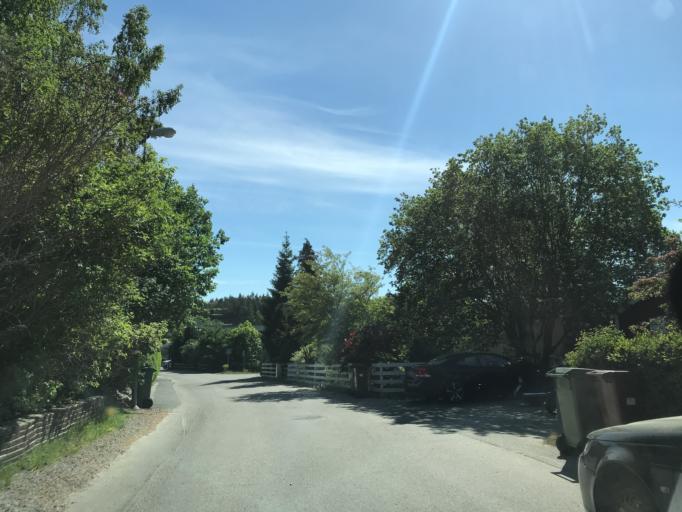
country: SE
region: Stockholm
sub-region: Jarfalla Kommun
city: Jakobsberg
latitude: 59.4527
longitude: 17.8912
